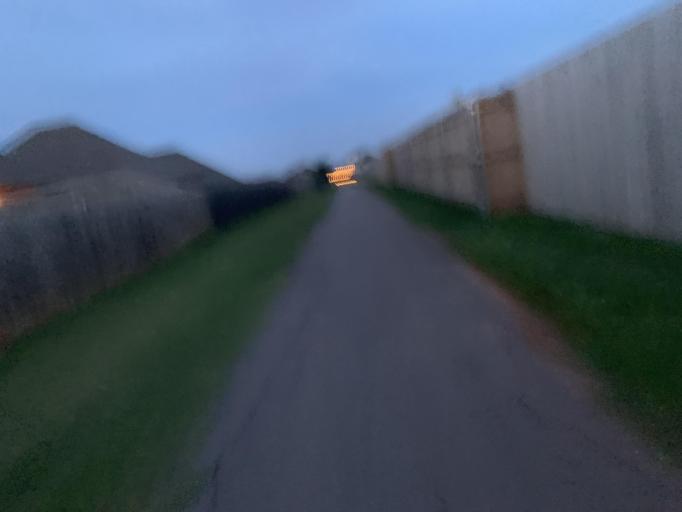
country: US
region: Oklahoma
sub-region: Oklahoma County
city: Edmond
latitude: 35.6622
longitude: -97.5747
